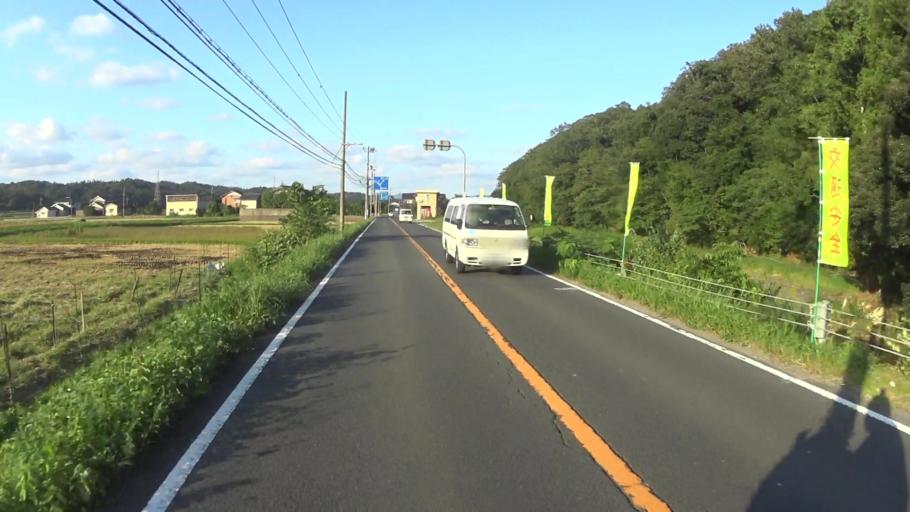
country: JP
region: Kyoto
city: Miyazu
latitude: 35.5967
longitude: 135.0444
